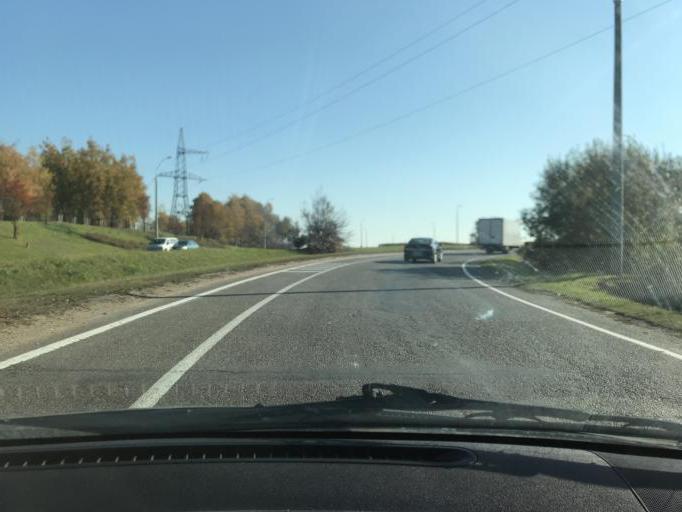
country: BY
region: Minsk
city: Syenitsa
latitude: 53.8364
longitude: 27.5348
